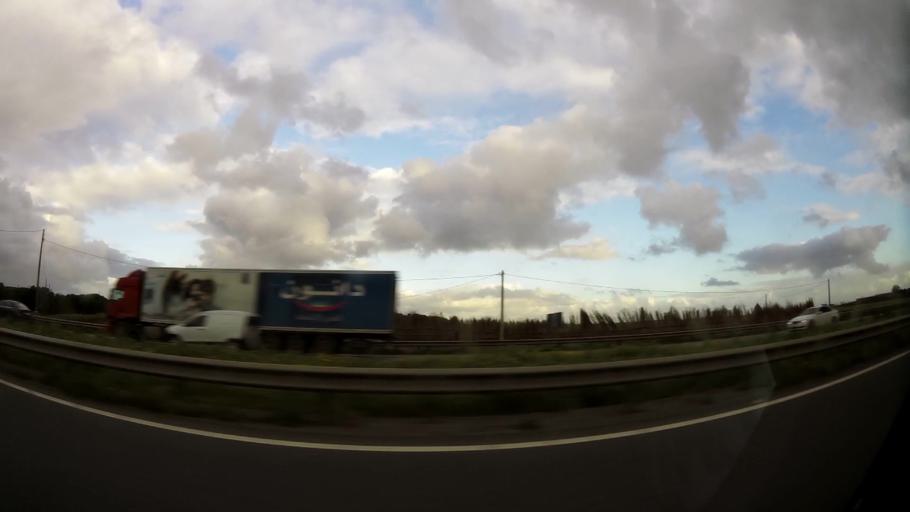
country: MA
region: Grand Casablanca
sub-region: Mediouna
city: Tit Mellil
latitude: 33.6023
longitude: -7.4376
